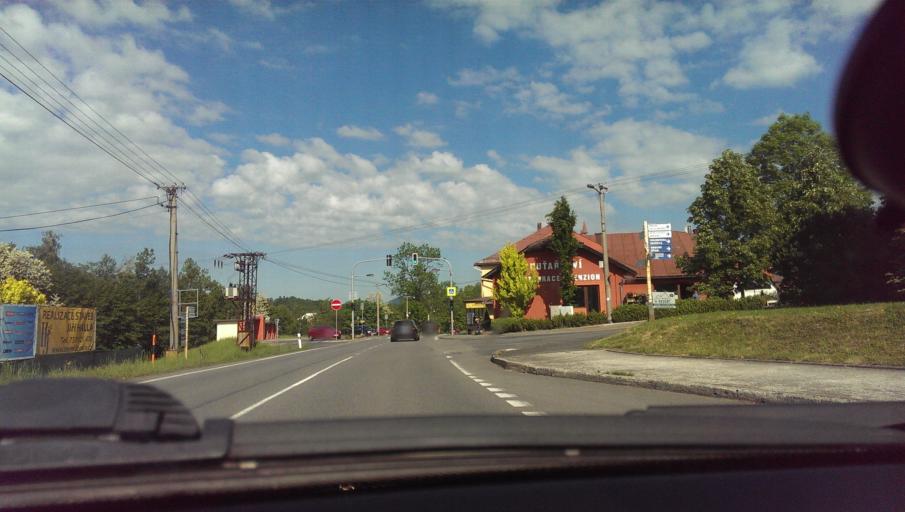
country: CZ
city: Kuncice pod Ondrejnikem
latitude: 49.5423
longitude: 18.2722
